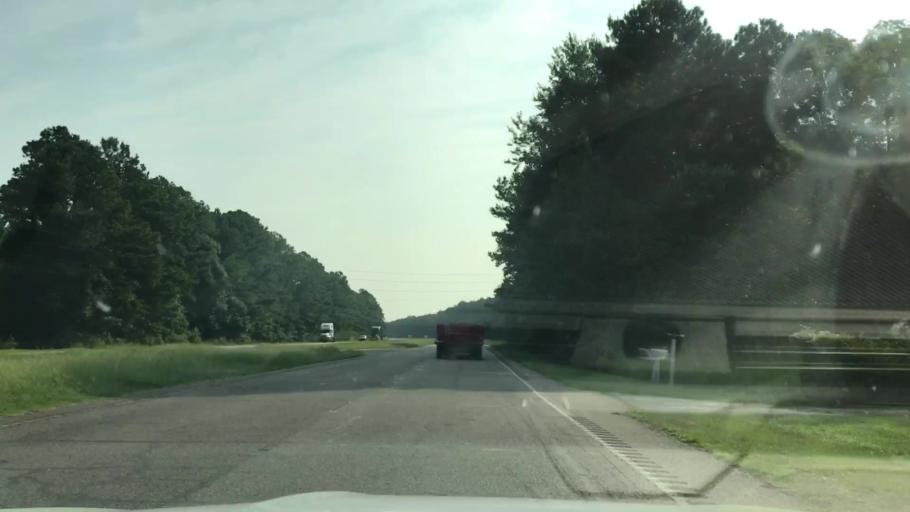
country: US
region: South Carolina
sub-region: Charleston County
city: Awendaw
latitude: 33.0783
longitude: -79.5070
